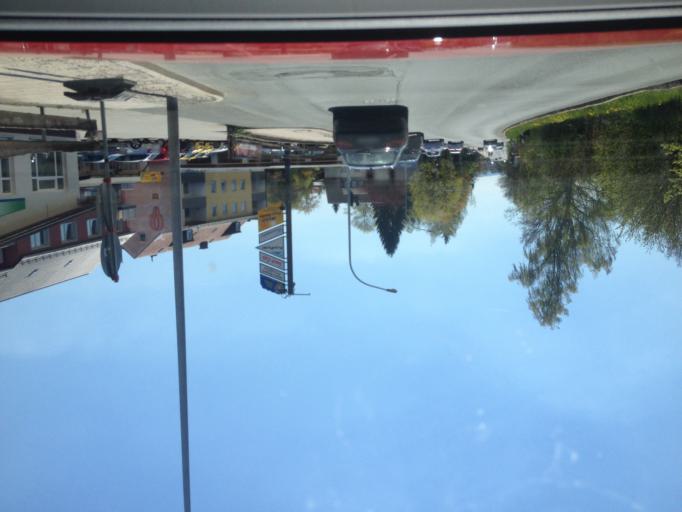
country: DE
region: Bavaria
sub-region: Upper Franconia
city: Hof
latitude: 50.2972
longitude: 11.9294
